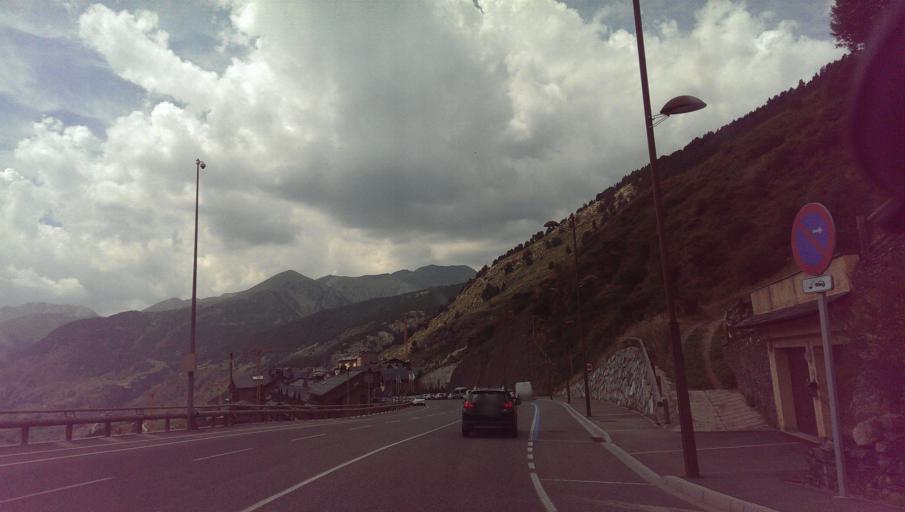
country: AD
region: Canillo
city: El Tarter
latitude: 42.5745
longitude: 1.6733
